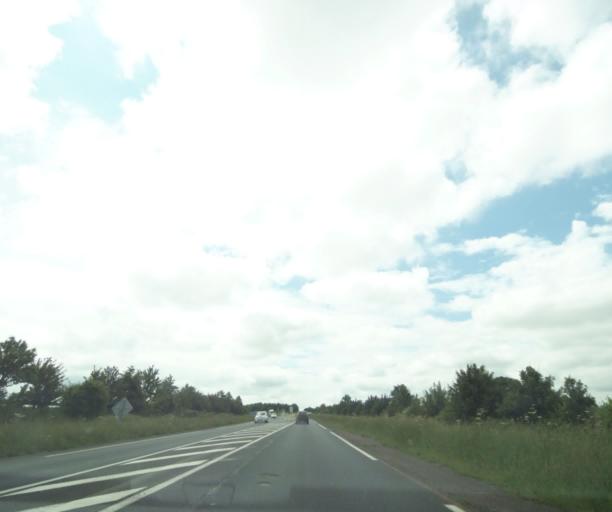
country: FR
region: Poitou-Charentes
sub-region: Departement des Deux-Sevres
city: Saint-Pardoux
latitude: 46.5501
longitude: -0.3109
